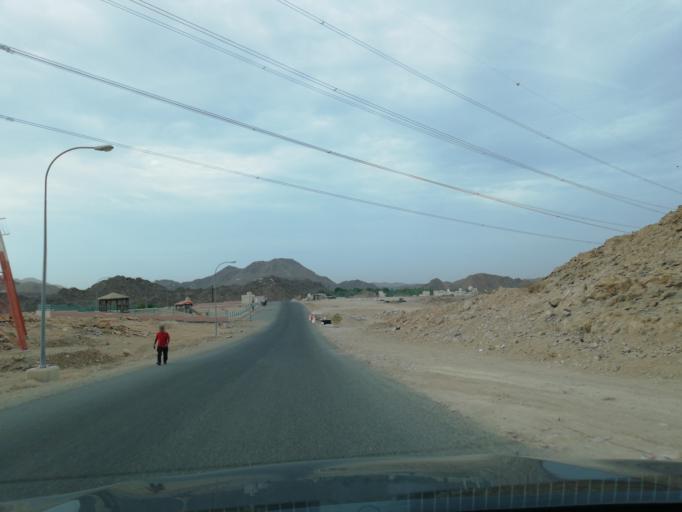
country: OM
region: Muhafazat Masqat
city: Bawshar
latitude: 23.4727
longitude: 58.3264
